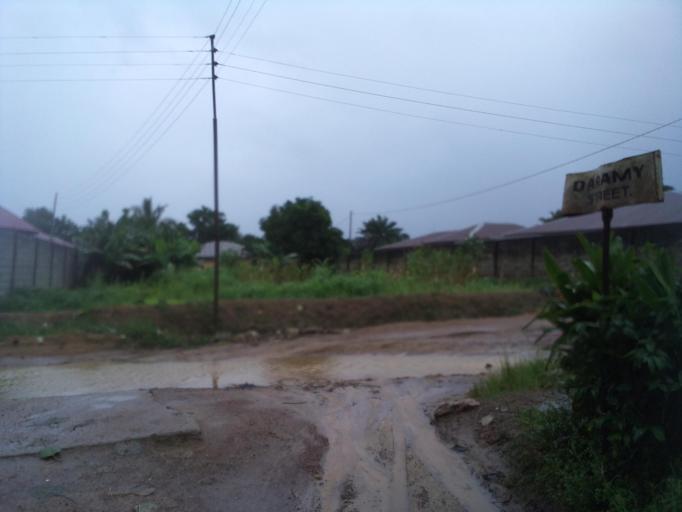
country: SL
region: Eastern Province
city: Kenema
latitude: 7.8566
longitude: -11.1923
